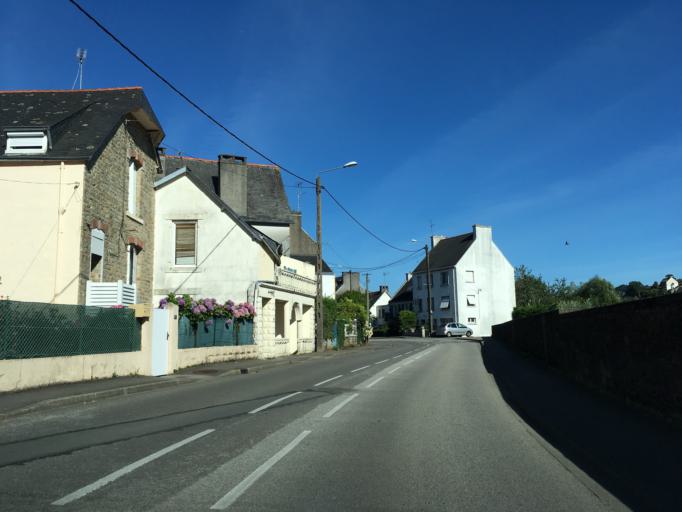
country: FR
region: Brittany
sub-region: Departement du Finistere
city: Quimper
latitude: 47.9958
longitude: -4.0888
